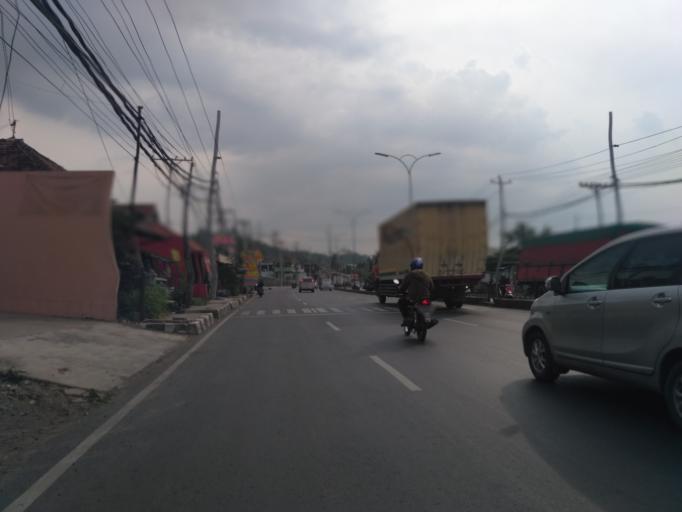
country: ID
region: Central Java
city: Semarang
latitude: -6.9861
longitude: 110.3438
